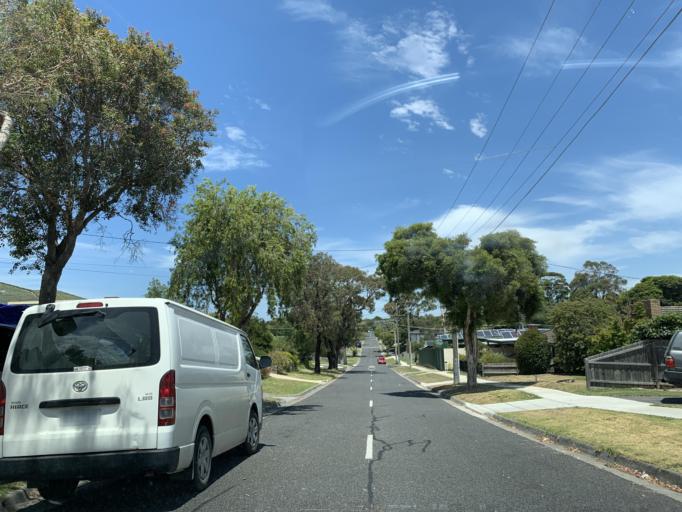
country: AU
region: Victoria
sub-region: Frankston
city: Langwarrin
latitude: -38.1482
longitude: 145.1876
